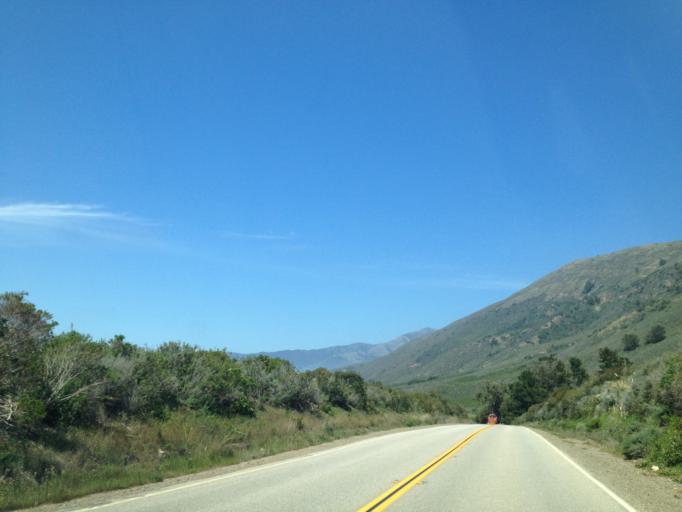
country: US
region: California
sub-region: Monterey County
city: King City
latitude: 35.9329
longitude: -121.4689
